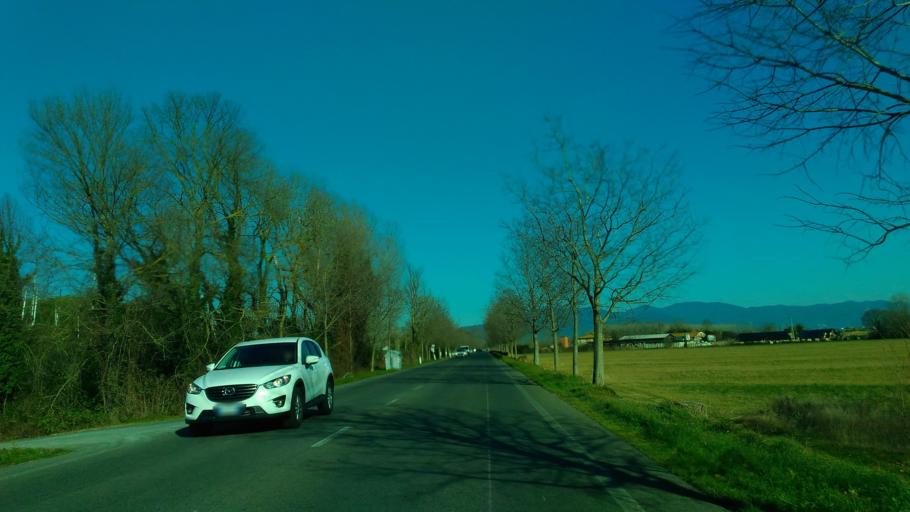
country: IT
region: Tuscany
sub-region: Province of Pisa
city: Marina di Pisa-Tirrenia-Calambrone
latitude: 43.6820
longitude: 10.3354
